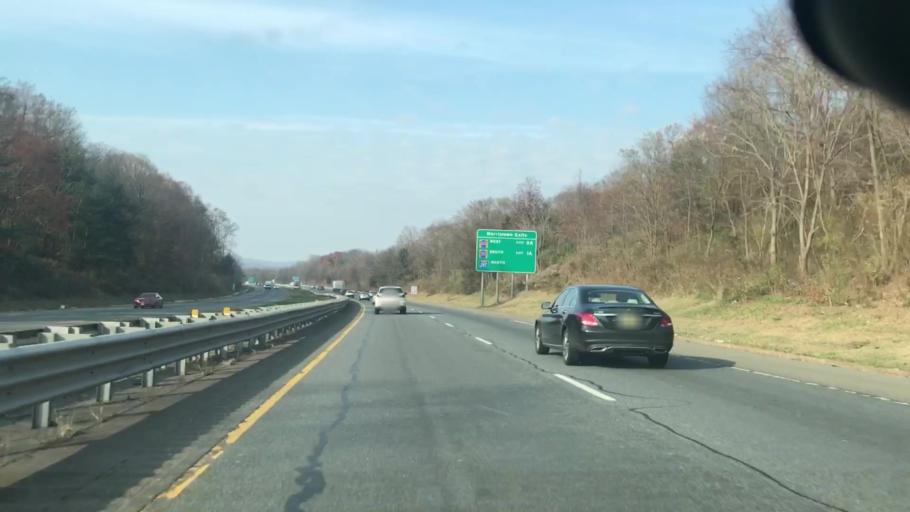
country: US
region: New Jersey
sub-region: Morris County
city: Madison
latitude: 40.7727
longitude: -74.4046
